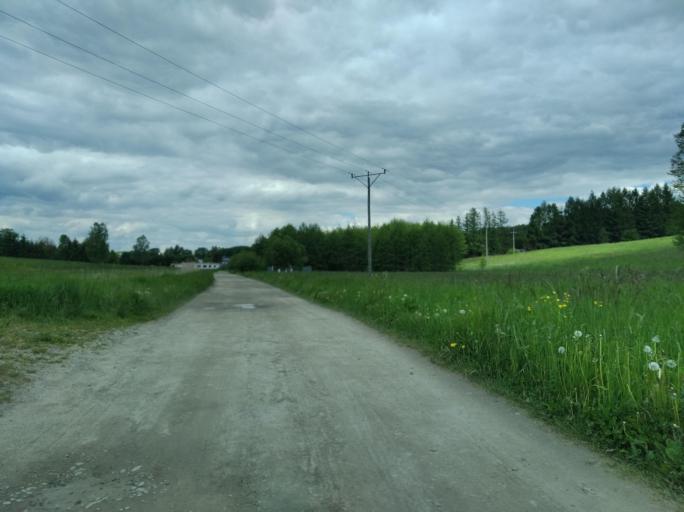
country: PL
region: Subcarpathian Voivodeship
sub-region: Powiat brzozowski
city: Zmiennica
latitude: 49.6737
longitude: 21.9723
